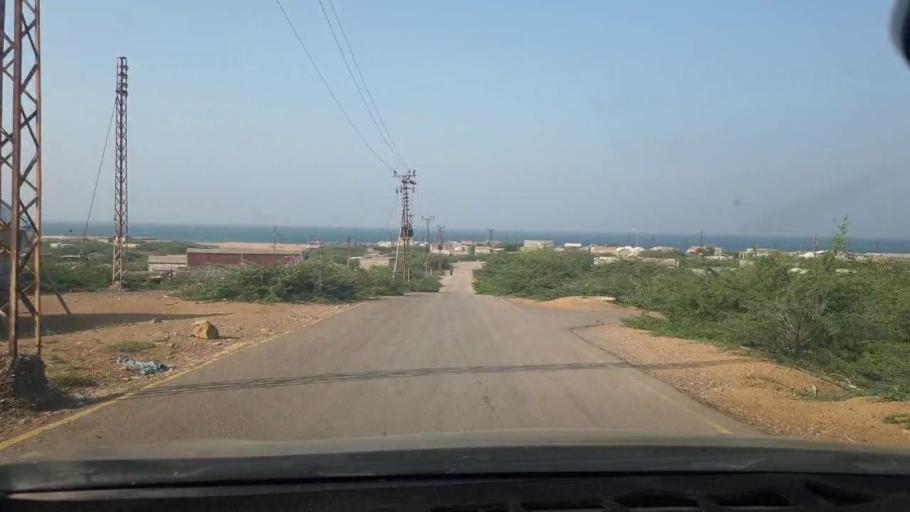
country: PK
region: Balochistan
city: Gadani
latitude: 24.8490
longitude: 66.6629
